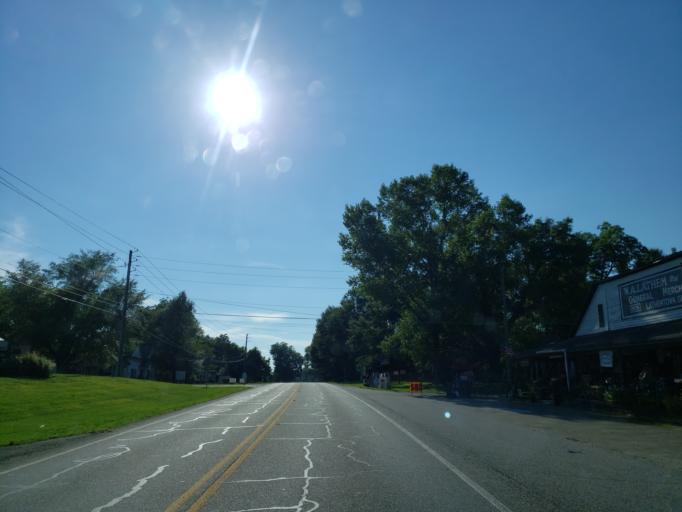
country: US
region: Georgia
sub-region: Fulton County
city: Milton
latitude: 34.2467
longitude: -84.3020
